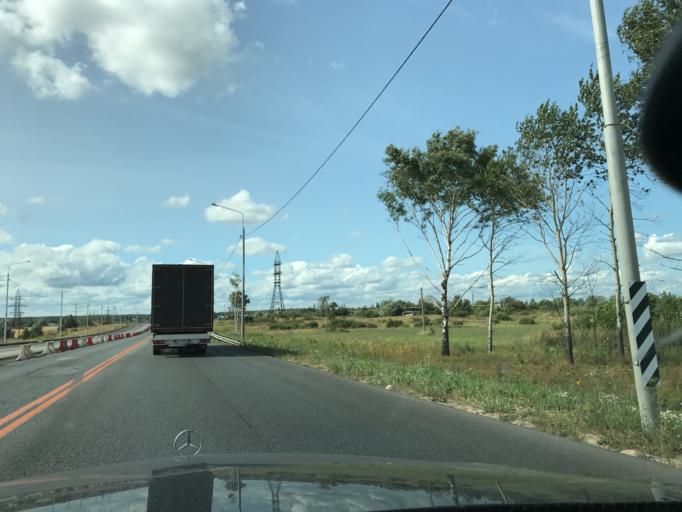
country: RU
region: Vladimir
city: Novovyazniki
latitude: 56.2184
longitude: 42.2027
